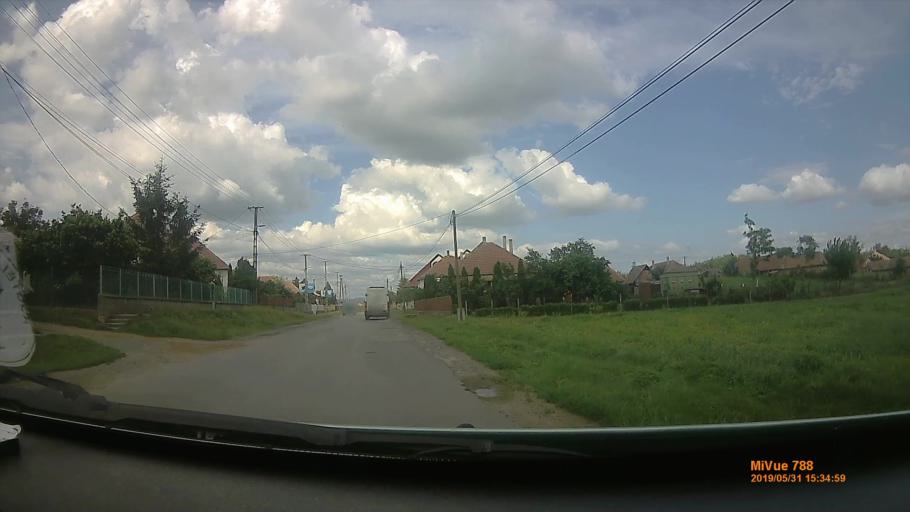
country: HU
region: Borsod-Abauj-Zemplen
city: Prugy
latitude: 48.0787
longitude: 21.2453
